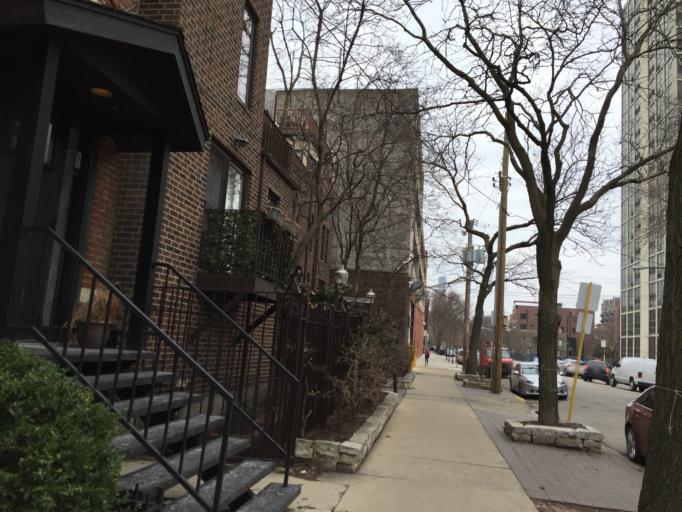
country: US
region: Illinois
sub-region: Cook County
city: Chicago
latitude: 41.9121
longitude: -87.6366
